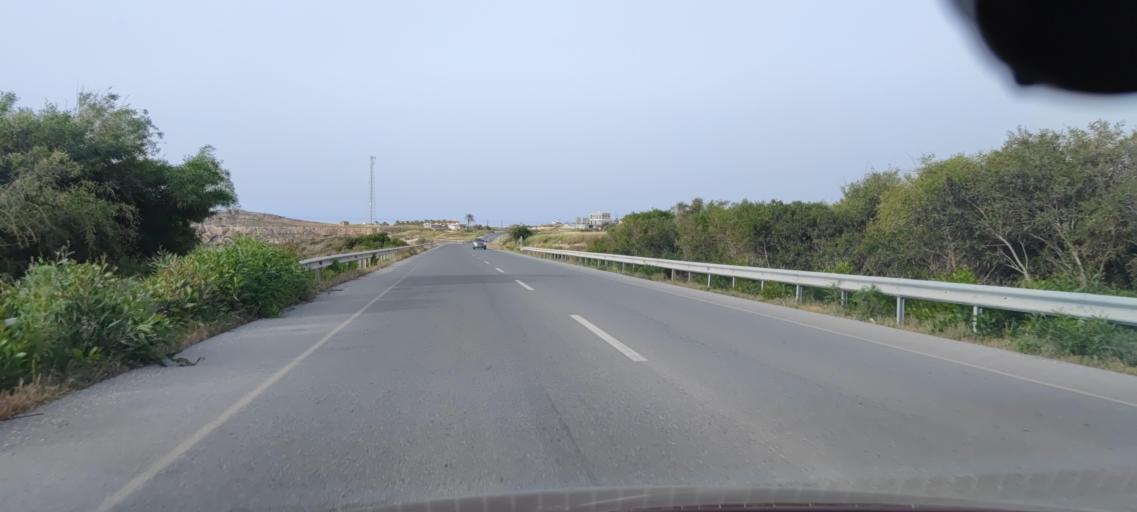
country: CY
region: Ammochostos
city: Rizokarpaso
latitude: 35.5647
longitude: 34.2474
